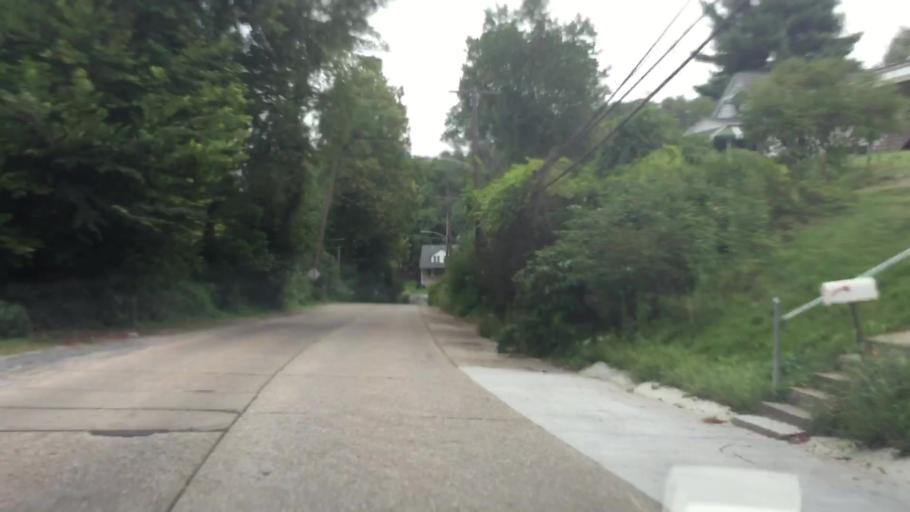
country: US
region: Pennsylvania
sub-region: Allegheny County
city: Heidelberg
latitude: 40.3926
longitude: -80.0836
